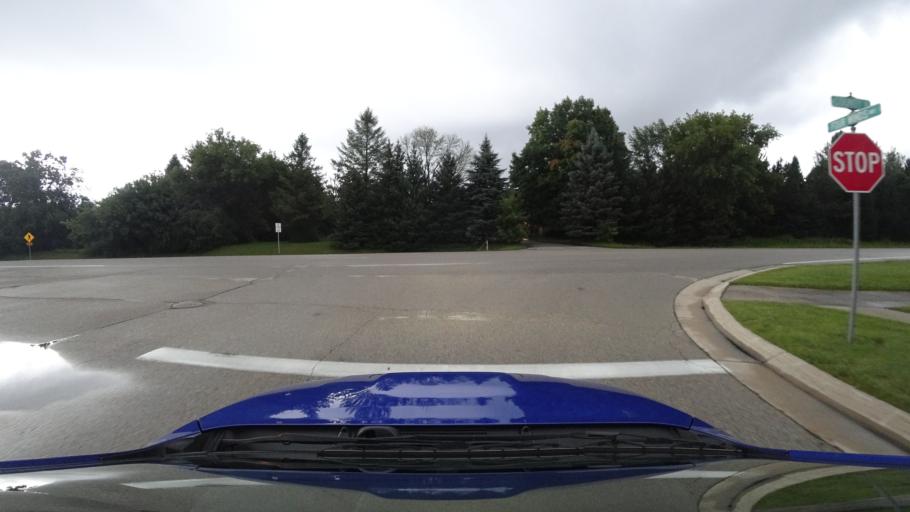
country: US
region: Wisconsin
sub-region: Waukesha County
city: Hartland
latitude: 43.1200
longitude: -88.3368
